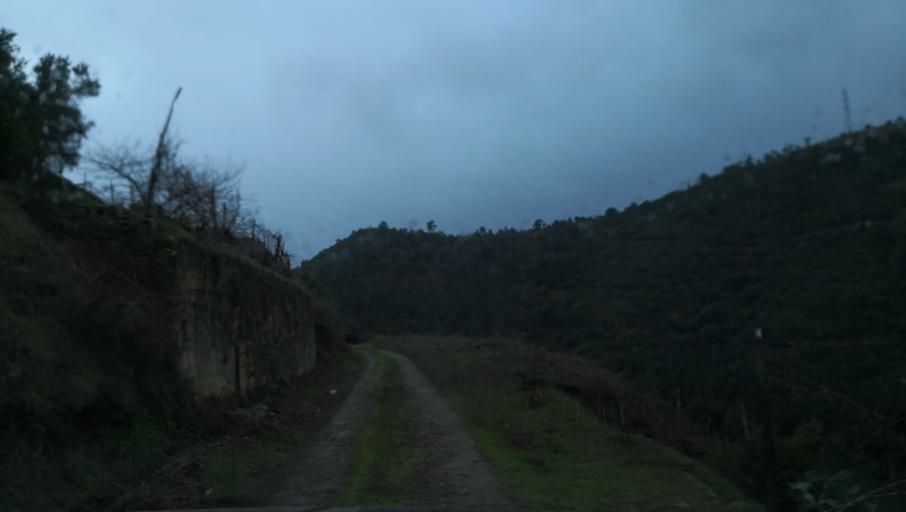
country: PT
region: Vila Real
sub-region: Santa Marta de Penaguiao
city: Santa Marta de Penaguiao
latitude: 41.2215
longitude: -7.7555
